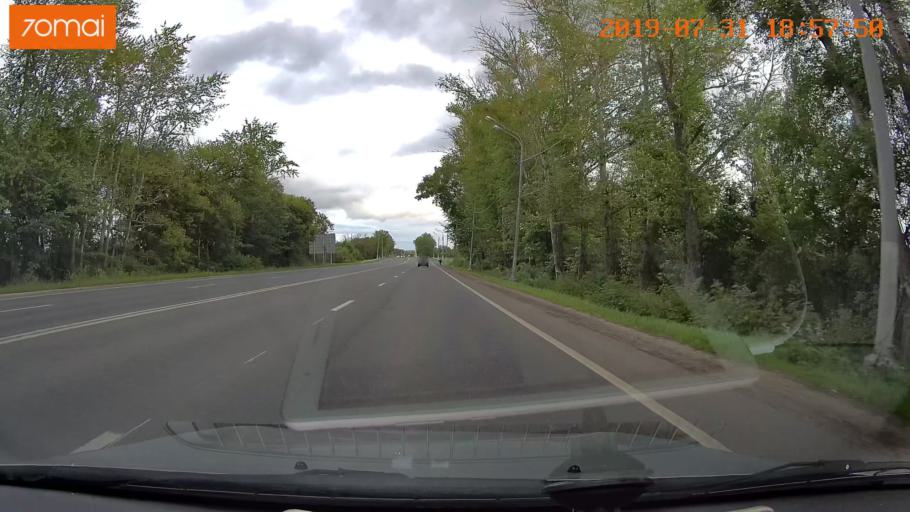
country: RU
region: Moskovskaya
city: Raduzhnyy
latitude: 55.1512
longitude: 38.6970
